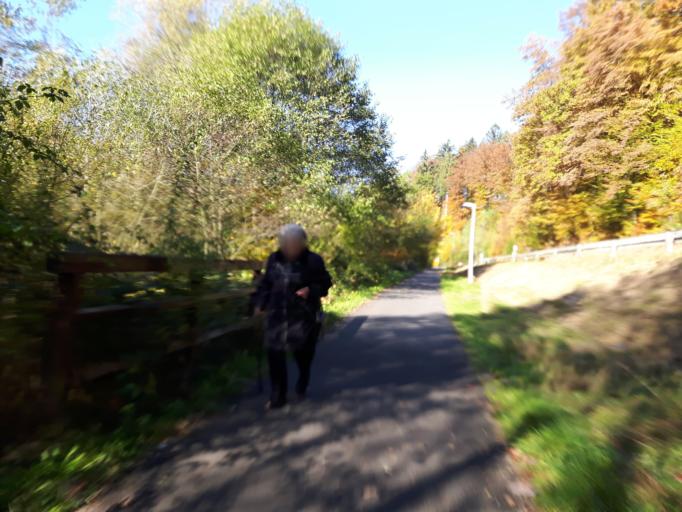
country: DE
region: Bavaria
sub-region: Regierungsbezirk Unterfranken
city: Heimbuchenthal
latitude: 49.9017
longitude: 9.3000
